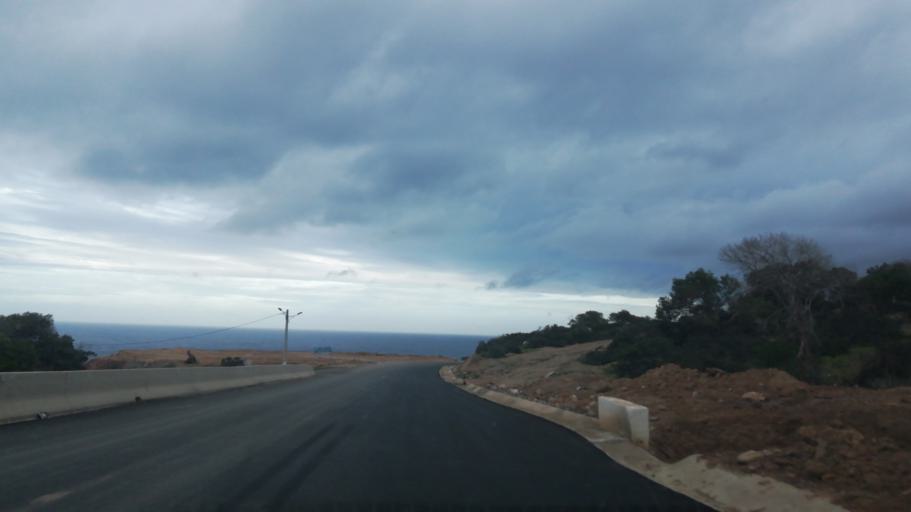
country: DZ
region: Oran
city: Bir el Djir
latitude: 35.7764
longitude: -0.5133
